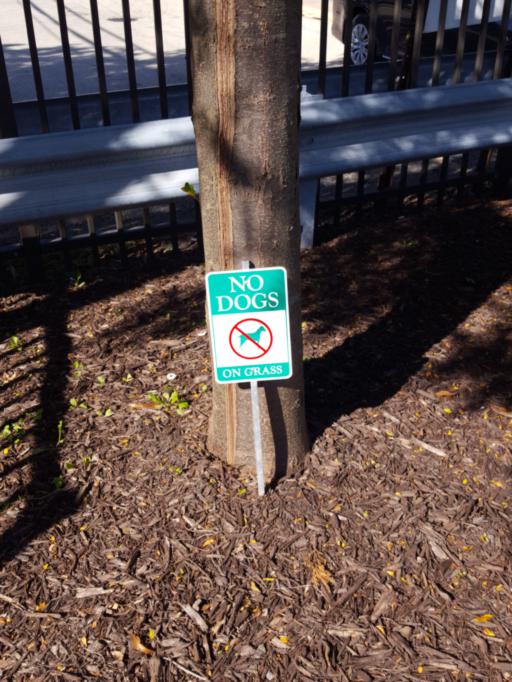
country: US
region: Illinois
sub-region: Cook County
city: Glenview
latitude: 42.0797
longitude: -87.7632
